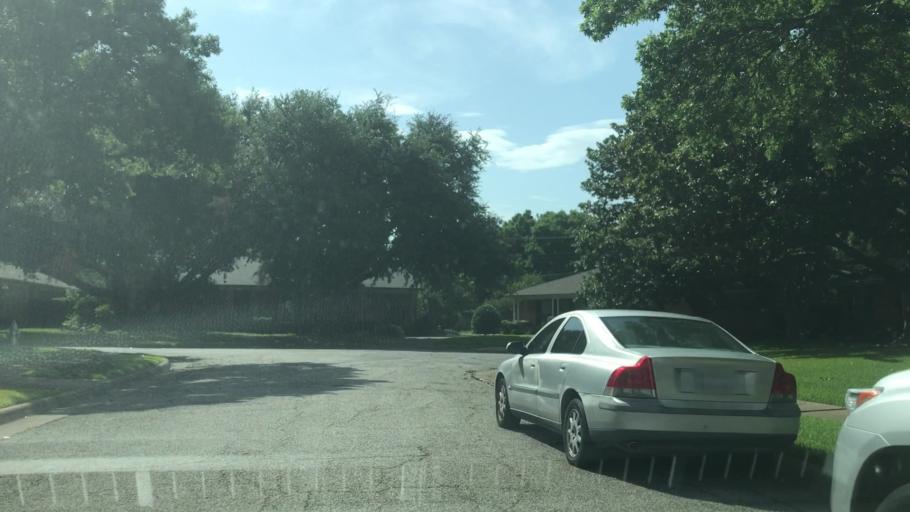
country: US
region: Texas
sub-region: Dallas County
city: Highland Park
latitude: 32.8546
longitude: -96.7574
